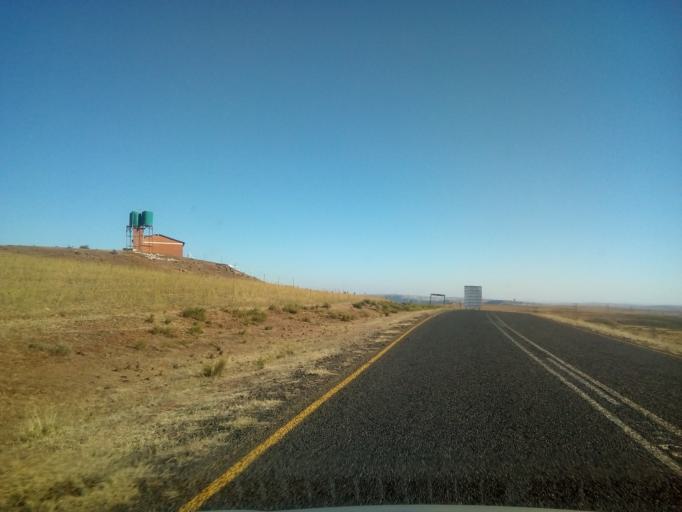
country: LS
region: Berea
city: Teyateyaneng
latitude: -29.2537
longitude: 27.7410
